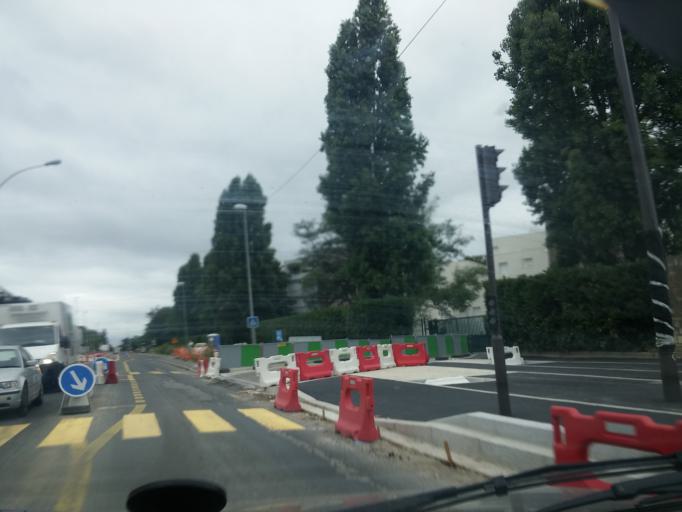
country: FR
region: Ile-de-France
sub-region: Departement du Val-de-Marne
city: Thiais
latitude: 48.7670
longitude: 2.3825
